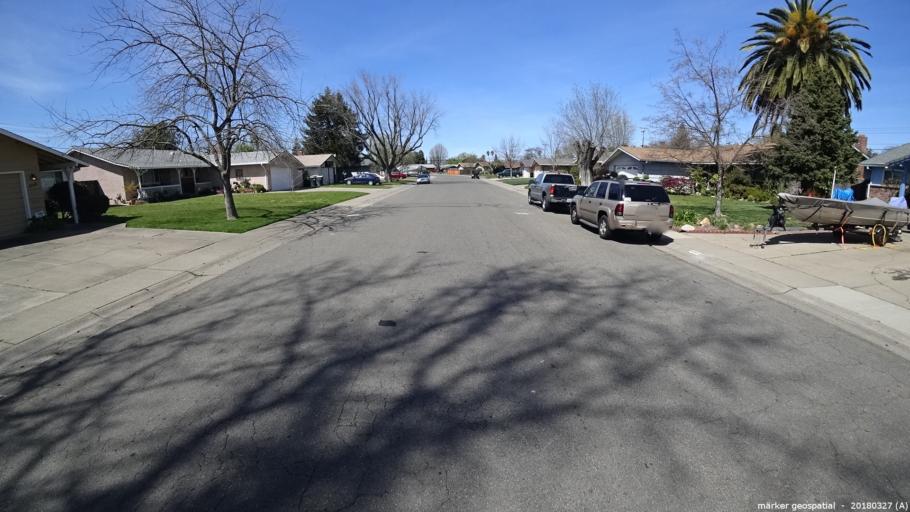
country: US
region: California
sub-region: Sacramento County
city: Rosemont
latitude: 38.5525
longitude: -121.3619
